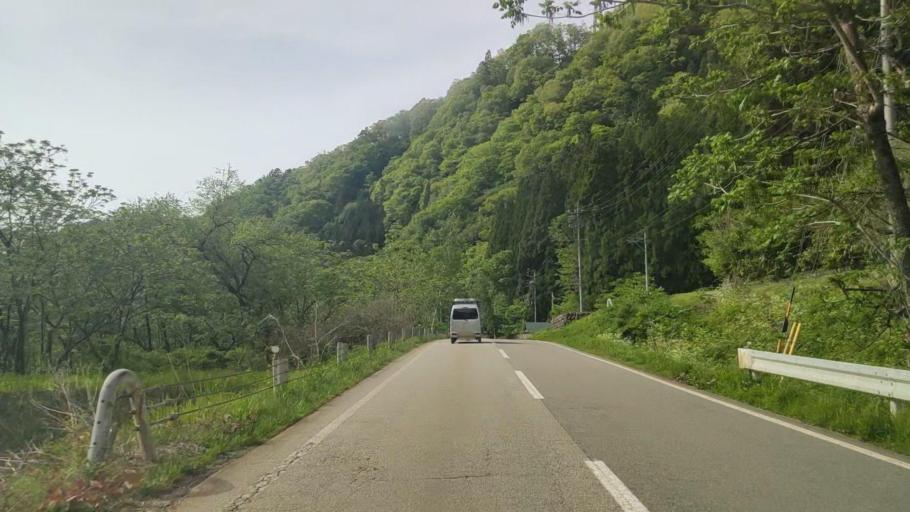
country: JP
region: Gifu
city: Takayama
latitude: 36.2631
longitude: 137.4311
